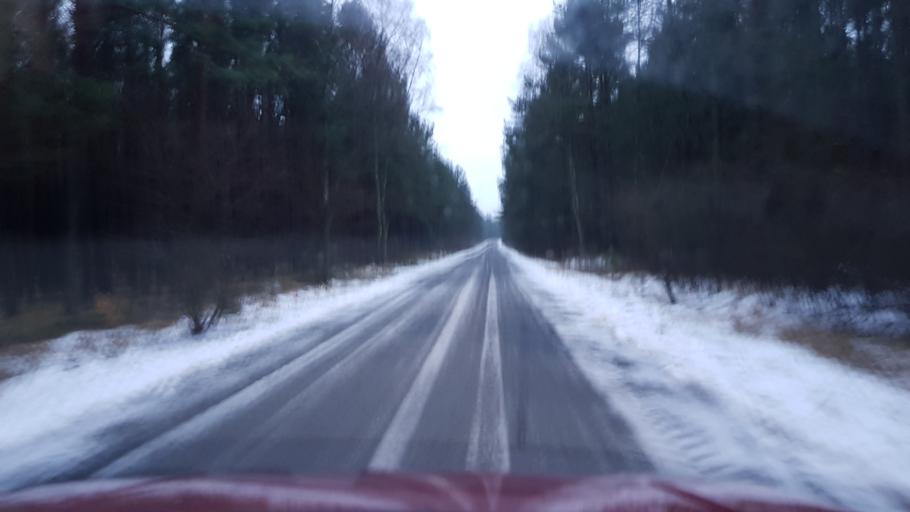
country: PL
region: West Pomeranian Voivodeship
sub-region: Powiat goleniowski
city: Goleniow
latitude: 53.4728
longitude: 14.8320
